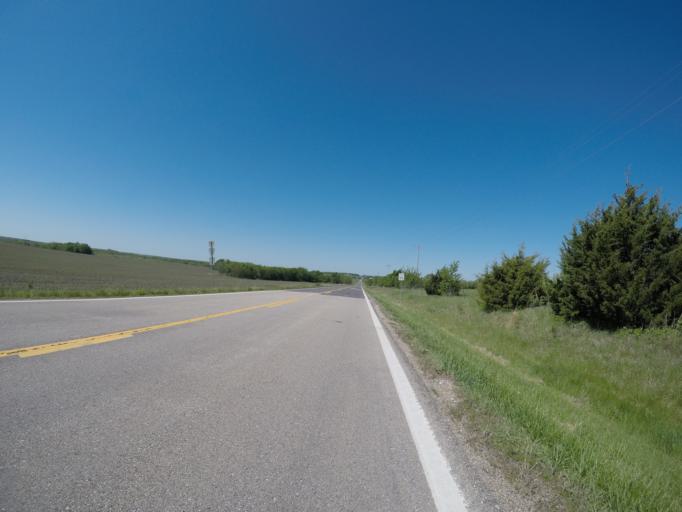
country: US
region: Kansas
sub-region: Osage County
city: Overbrook
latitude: 38.8871
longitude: -95.4299
